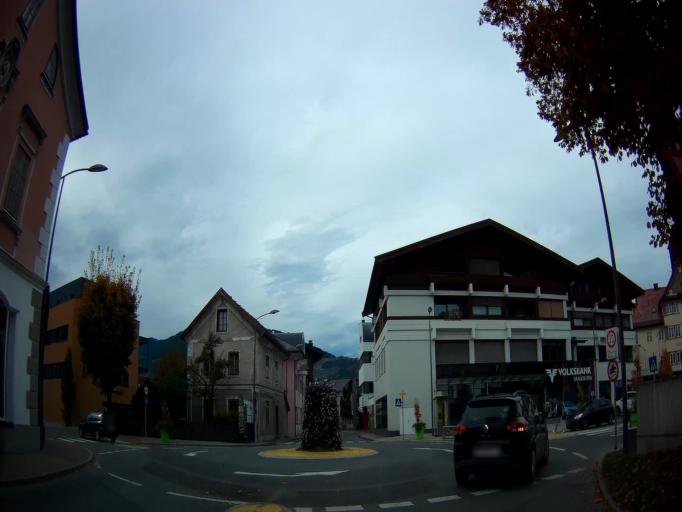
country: AT
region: Salzburg
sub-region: Politischer Bezirk Zell am See
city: Saalfelden am Steinernen Meer
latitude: 47.4268
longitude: 12.8458
